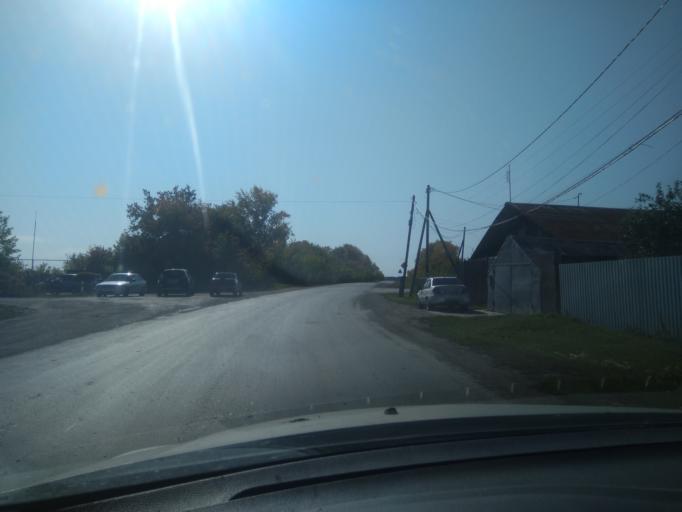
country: RU
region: Sverdlovsk
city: Pokrovskoye
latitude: 56.4631
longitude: 61.6144
